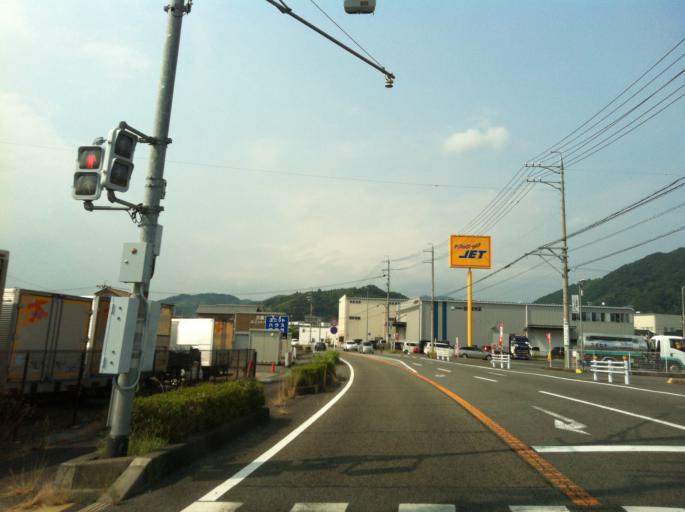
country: JP
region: Shizuoka
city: Fujieda
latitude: 34.8998
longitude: 138.2852
